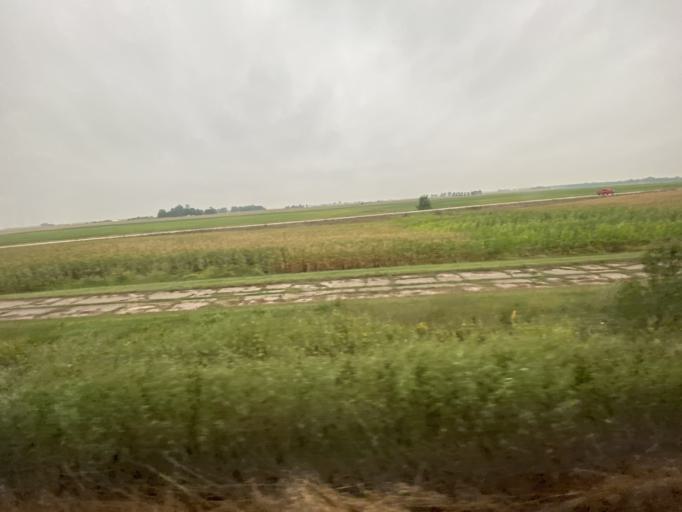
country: US
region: Illinois
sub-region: DeKalb County
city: Somonauk
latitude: 41.6245
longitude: -88.7372
